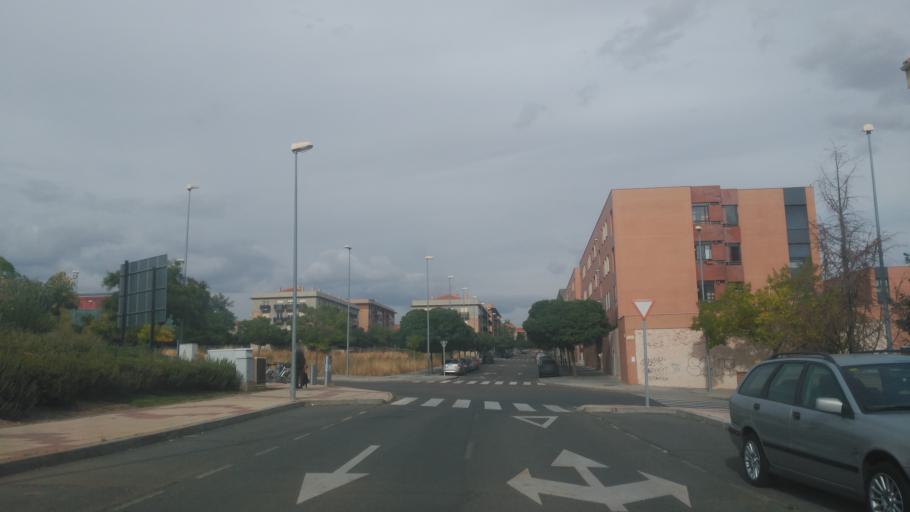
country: ES
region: Castille and Leon
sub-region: Provincia de Salamanca
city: Salamanca
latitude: 40.9674
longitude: -5.6839
